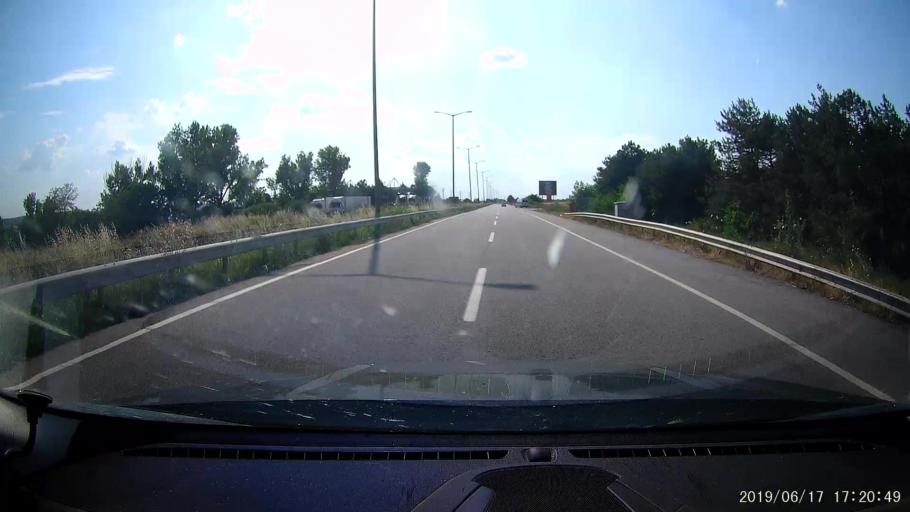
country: GR
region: East Macedonia and Thrace
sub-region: Nomos Evrou
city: Rizia
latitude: 41.7033
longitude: 26.4067
